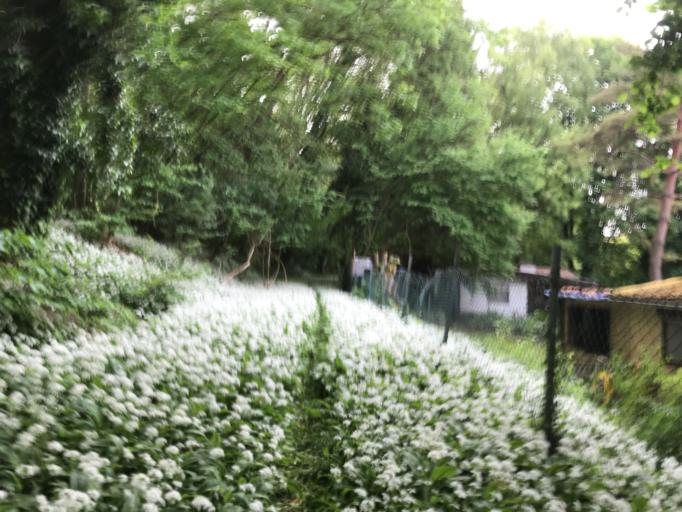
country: DE
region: Rheinland-Pfalz
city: Engelstadt
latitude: 49.8911
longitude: 8.0689
